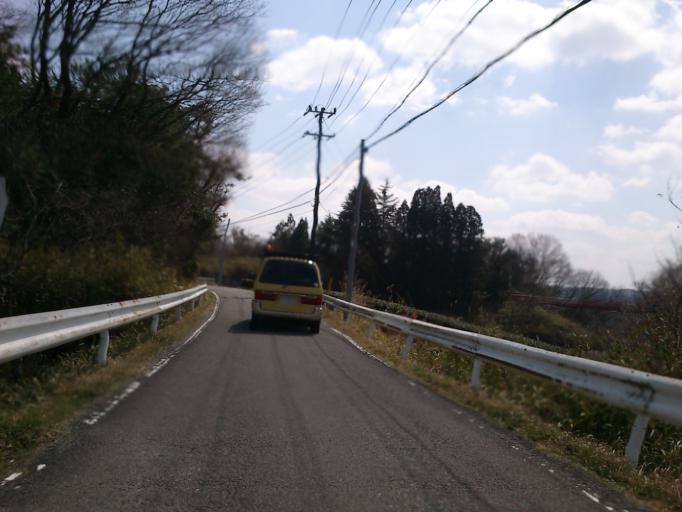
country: JP
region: Mie
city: Nabari
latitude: 34.7144
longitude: 136.0271
